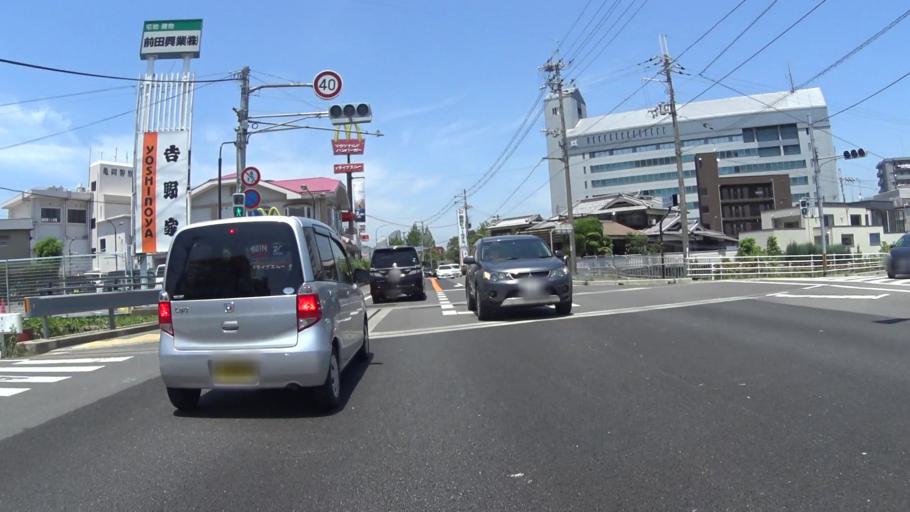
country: JP
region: Kyoto
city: Kameoka
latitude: 35.0121
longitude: 135.5739
